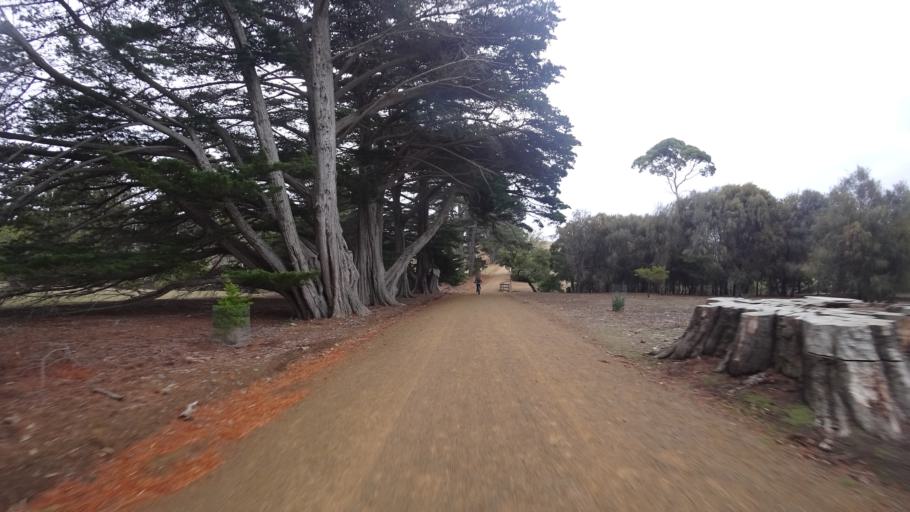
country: AU
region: Tasmania
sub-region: Sorell
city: Sorell
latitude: -42.5825
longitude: 148.0640
